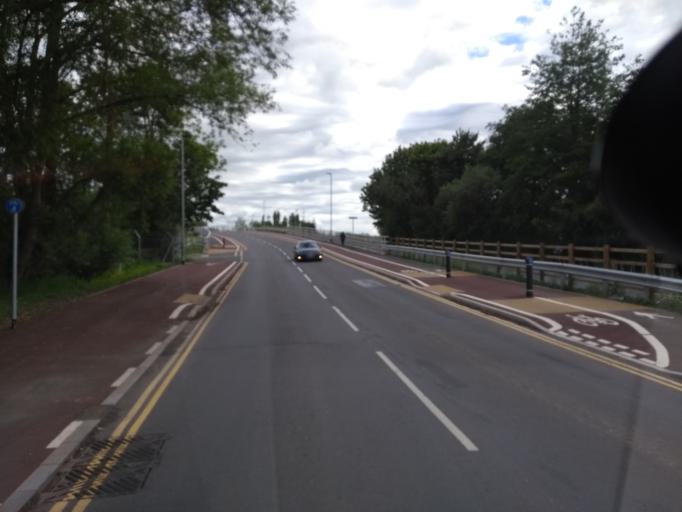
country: GB
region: England
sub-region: Somerset
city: Bridgwater
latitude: 51.1117
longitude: -2.9898
